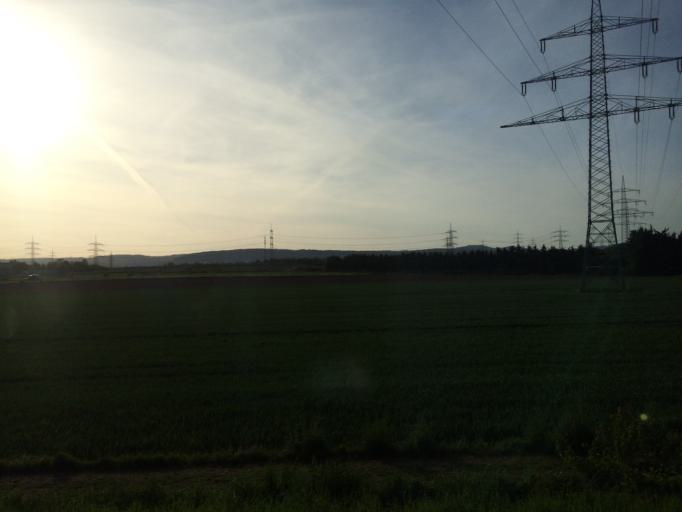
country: DE
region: Hesse
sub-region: Regierungsbezirk Darmstadt
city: Hattersheim
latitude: 50.0768
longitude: 8.5000
